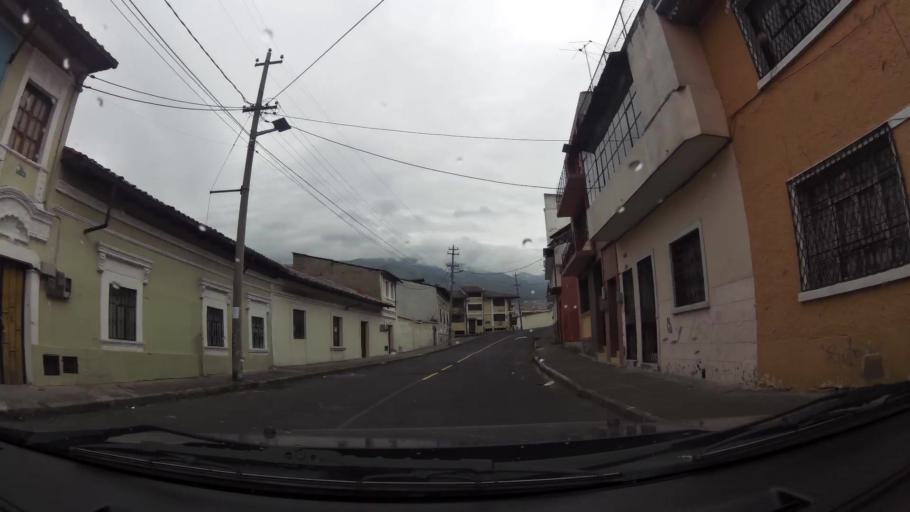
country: EC
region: Pichincha
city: Quito
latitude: -0.2292
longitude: -78.5099
